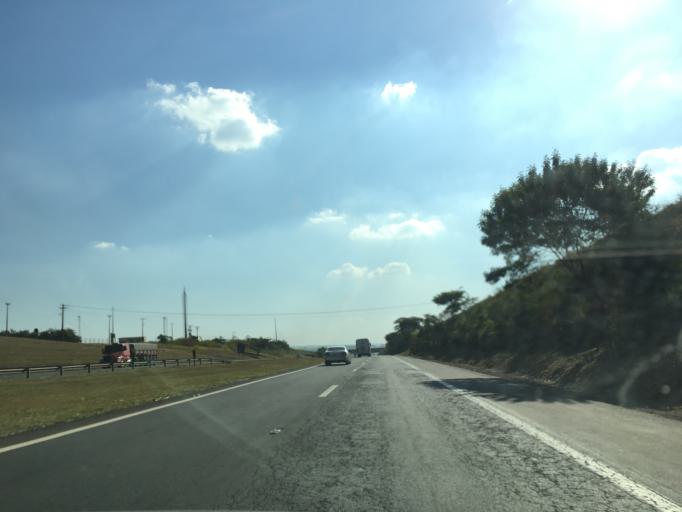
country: BR
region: Sao Paulo
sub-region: Santa Barbara D'Oeste
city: Santa Barbara d'Oeste
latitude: -22.7618
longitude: -47.4572
